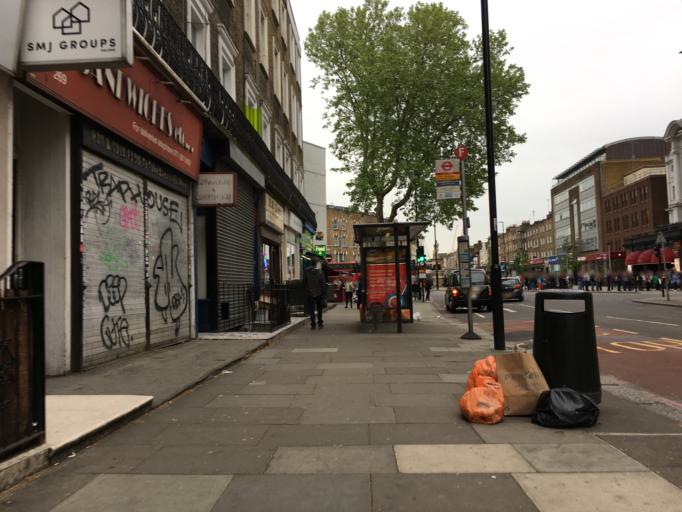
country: GB
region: England
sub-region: Greater London
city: Camden Town
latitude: 51.5341
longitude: -0.1382
